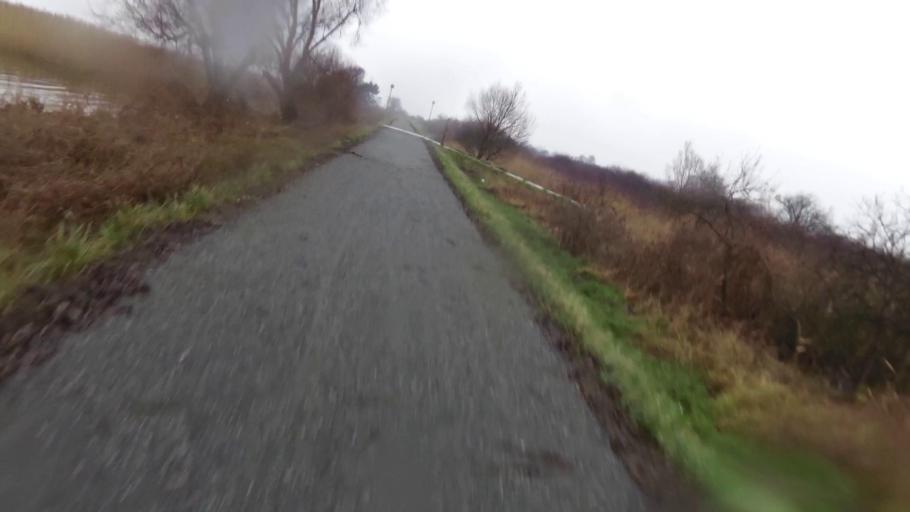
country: PL
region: West Pomeranian Voivodeship
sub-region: Powiat policki
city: Police
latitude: 53.4893
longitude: 14.6947
